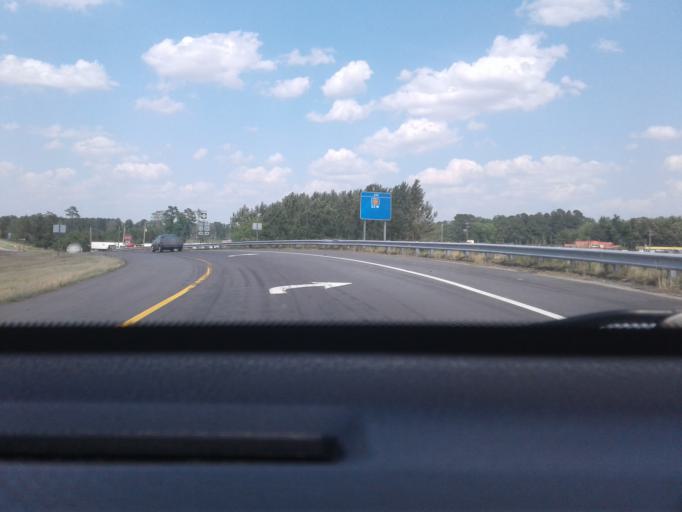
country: US
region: North Carolina
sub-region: Cumberland County
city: Eastover
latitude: 35.1221
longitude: -78.7533
